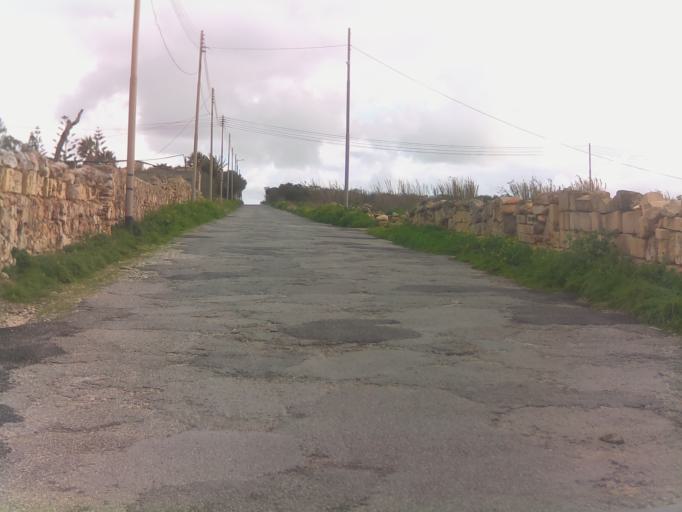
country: MT
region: Il-Mellieha
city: Mellieha
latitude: 35.9906
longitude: 14.3644
